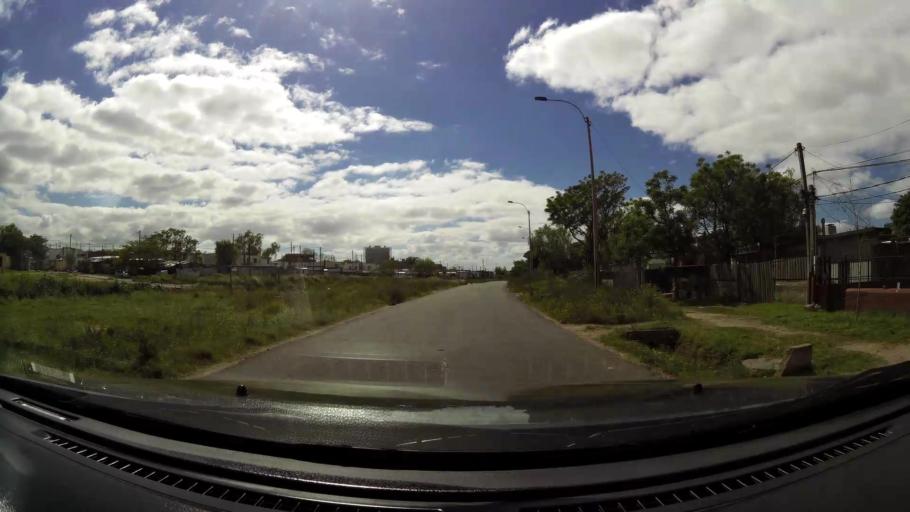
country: UY
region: Montevideo
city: Montevideo
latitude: -34.8822
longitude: -56.1260
